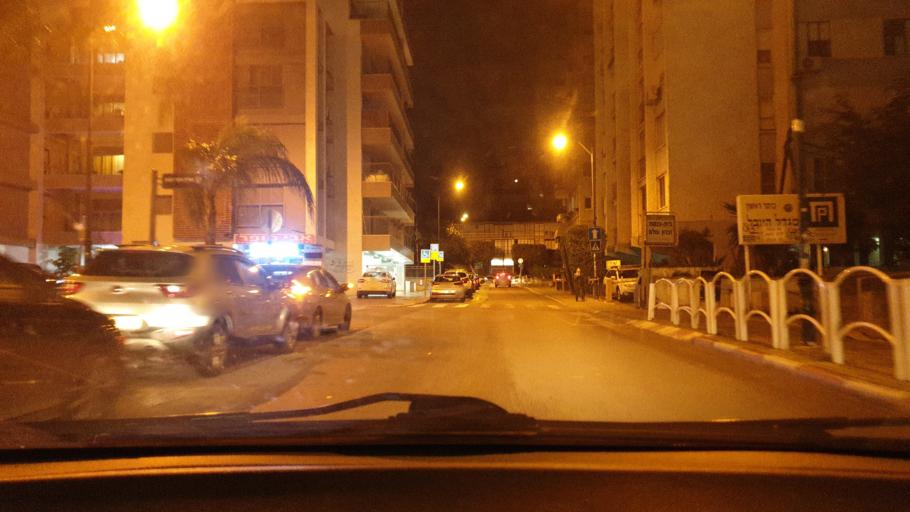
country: IL
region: Central District
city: Rishon LeZiyyon
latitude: 31.9668
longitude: 34.8036
